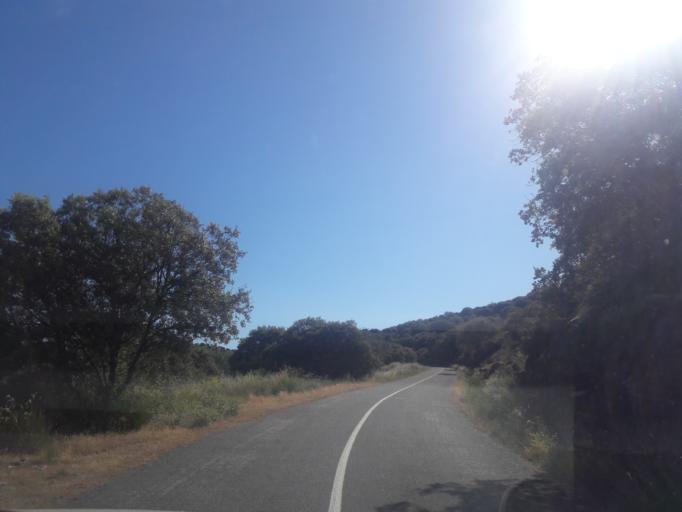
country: ES
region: Castille and Leon
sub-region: Provincia de Salamanca
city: Saucelle
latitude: 41.0346
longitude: -6.7697
